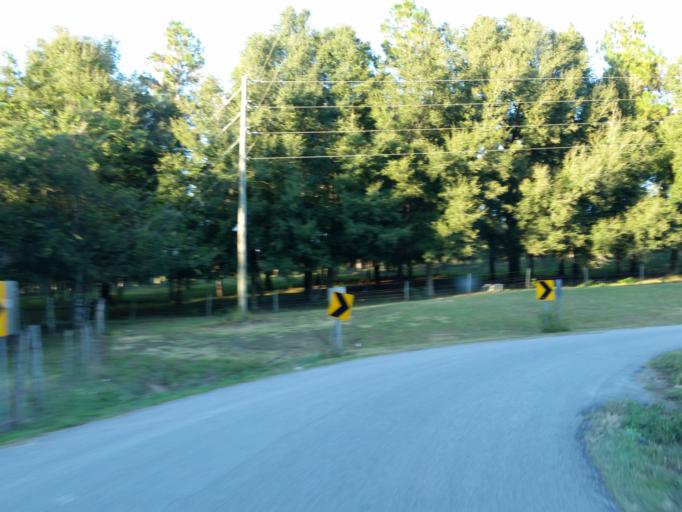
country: US
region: Florida
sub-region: Hernando County
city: Hill 'n Dale
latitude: 28.4566
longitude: -82.2698
